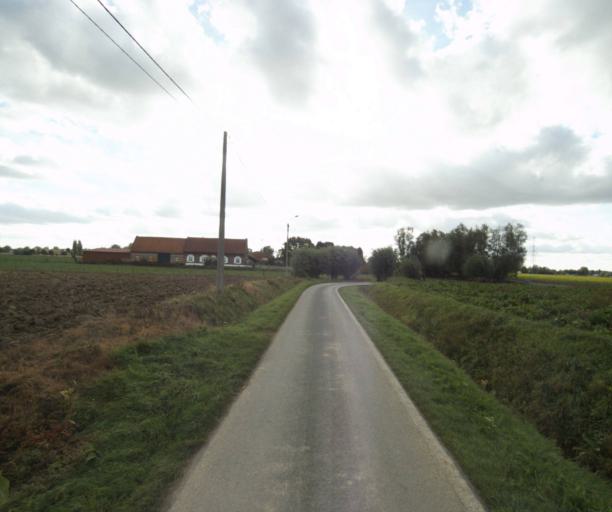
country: FR
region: Nord-Pas-de-Calais
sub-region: Departement du Nord
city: Houplines
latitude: 50.6719
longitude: 2.9209
